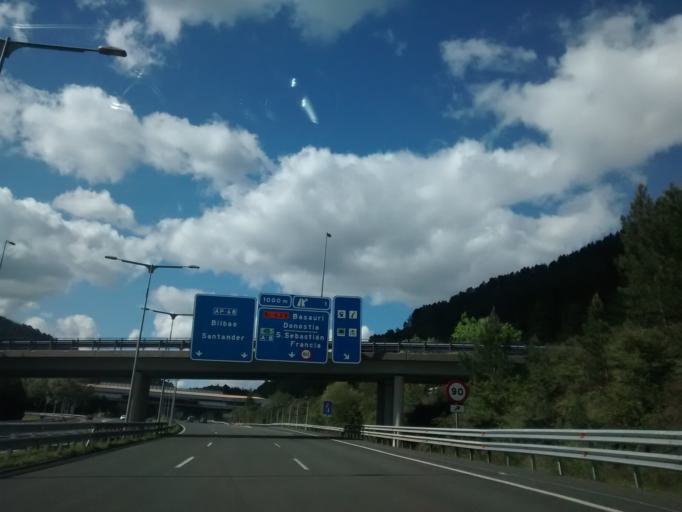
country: ES
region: Basque Country
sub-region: Bizkaia
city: Arrigorriaga
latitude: 43.1883
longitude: -2.8945
